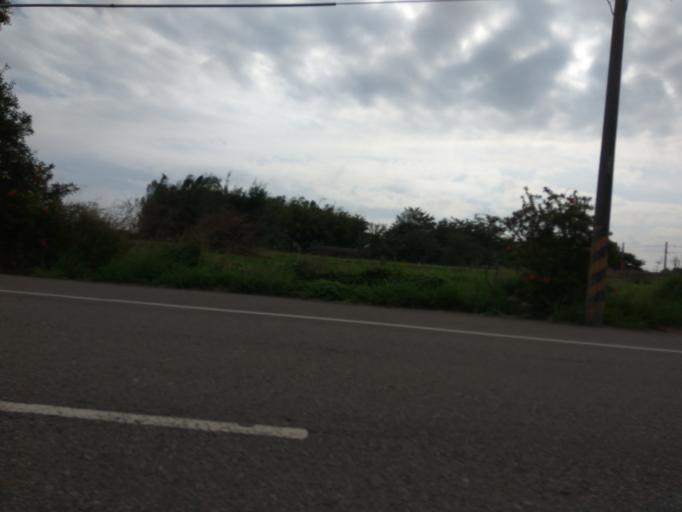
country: TW
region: Taiwan
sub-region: Hsinchu
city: Zhubei
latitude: 24.9703
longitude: 121.0227
